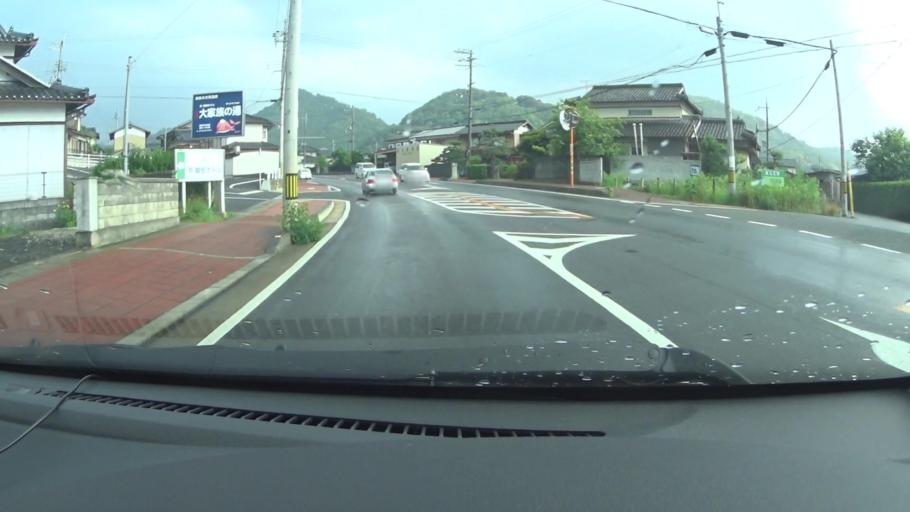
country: JP
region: Kyoto
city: Ayabe
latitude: 35.2953
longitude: 135.2668
